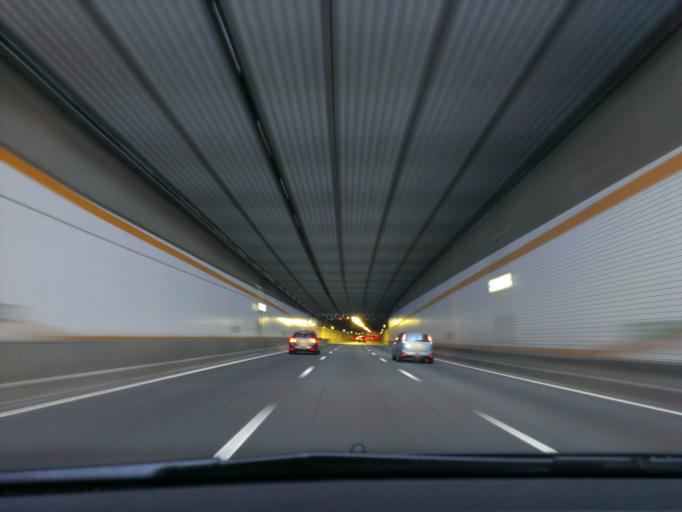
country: NL
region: South Holland
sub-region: Gemeente Barendrecht
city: Barendrecht
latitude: 51.8363
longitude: 4.5137
